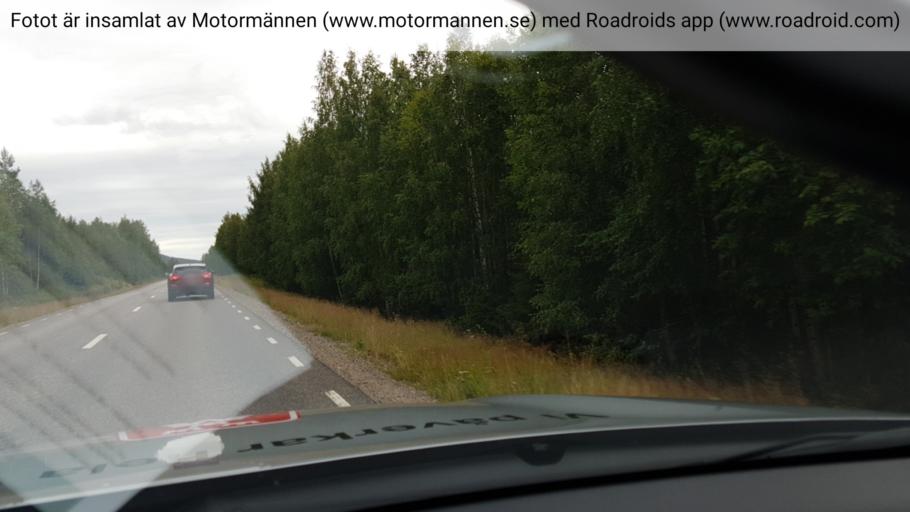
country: SE
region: Norrbotten
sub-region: Overkalix Kommun
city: OEverkalix
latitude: 66.5856
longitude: 22.7566
